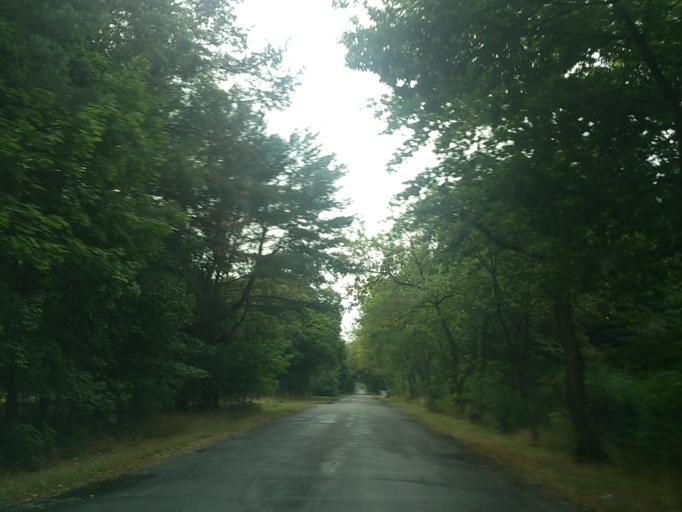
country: PL
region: Greater Poland Voivodeship
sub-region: Powiat poznanski
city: Kobylnica
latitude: 52.5192
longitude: 17.1564
